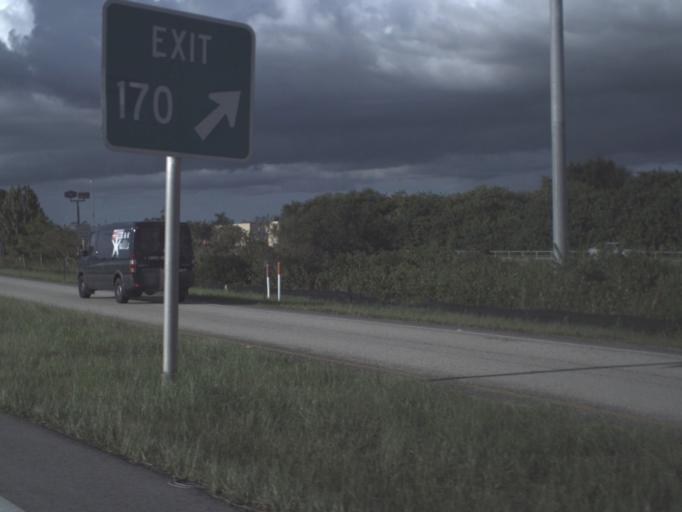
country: US
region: Florida
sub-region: Charlotte County
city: Harbour Heights
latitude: 27.0171
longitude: -82.0463
